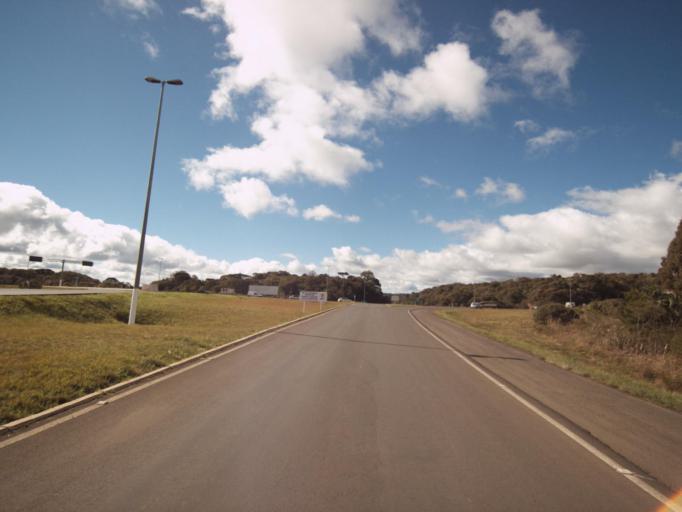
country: BR
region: Santa Catarina
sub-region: Concordia
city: Concordia
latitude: -26.9702
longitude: -51.8555
